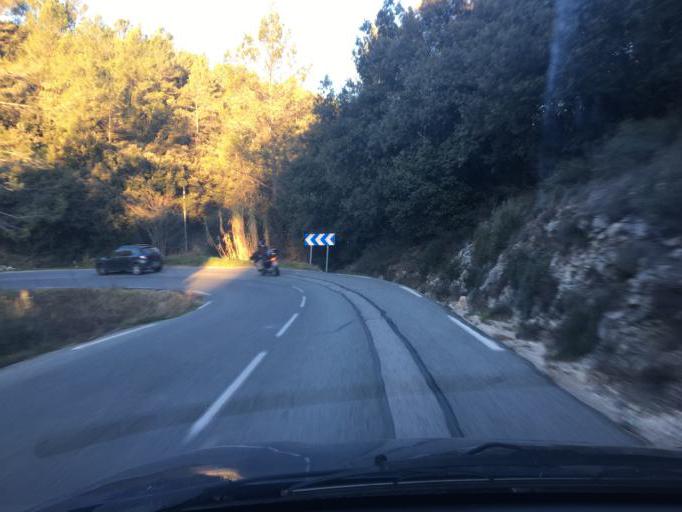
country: FR
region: Provence-Alpes-Cote d'Azur
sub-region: Departement du Var
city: Taradeau
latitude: 43.4580
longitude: 6.4198
